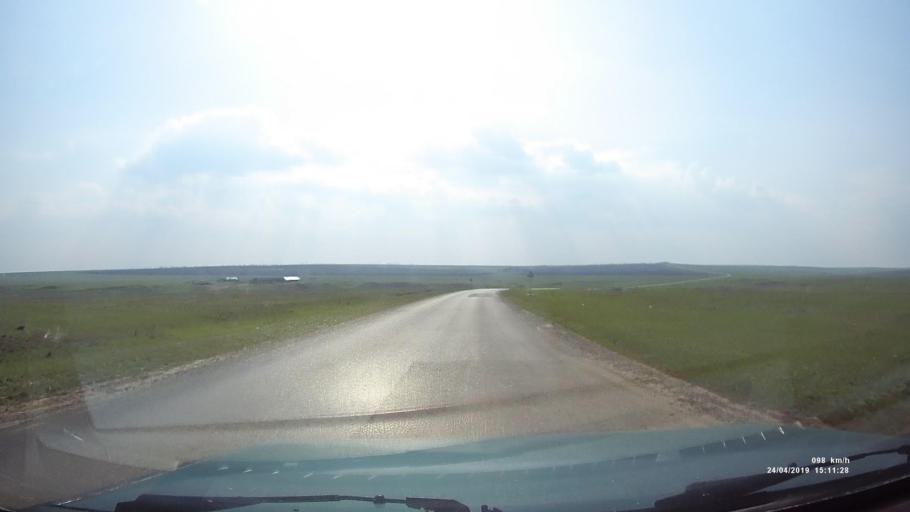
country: RU
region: Rostov
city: Remontnoye
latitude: 46.5443
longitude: 43.3205
